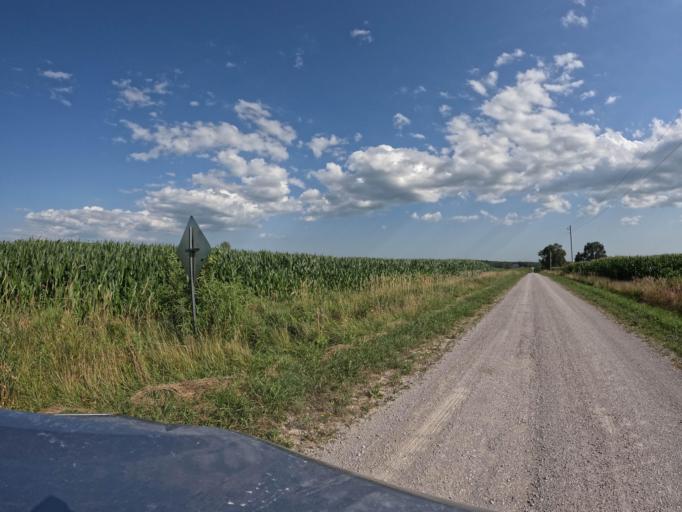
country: US
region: Iowa
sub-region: Appanoose County
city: Centerville
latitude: 40.7162
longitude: -93.0306
